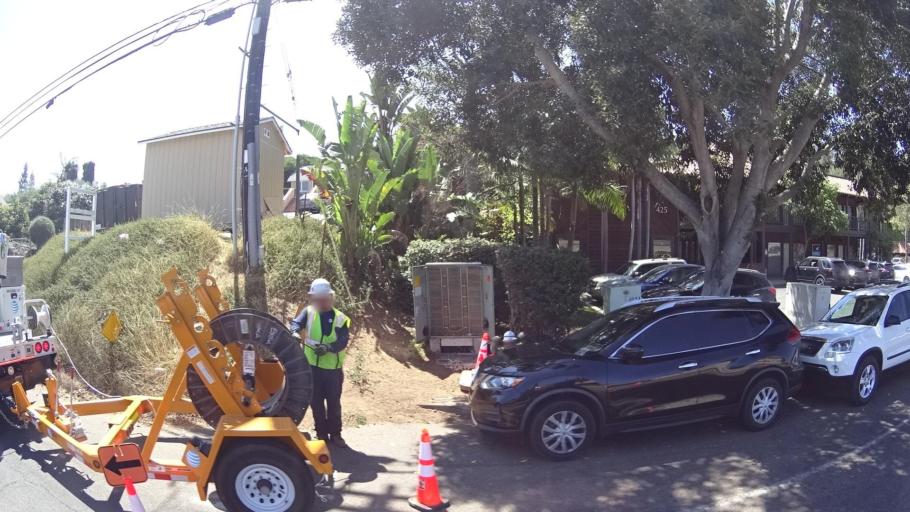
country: US
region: California
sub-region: San Diego County
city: Fallbrook
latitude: 33.3820
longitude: -117.2476
